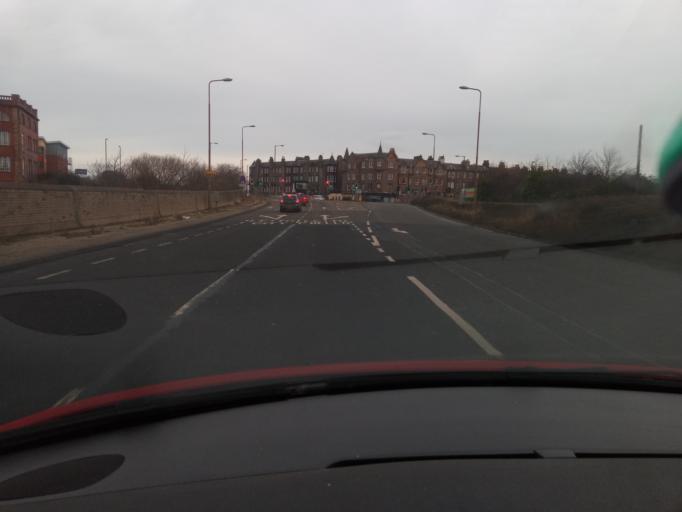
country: GB
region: Scotland
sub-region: West Lothian
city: Seafield
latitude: 55.9564
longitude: -3.1231
